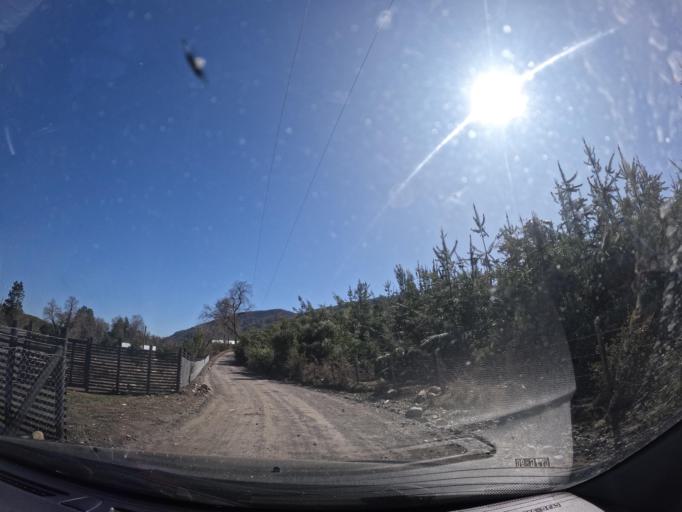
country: CL
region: Maule
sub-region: Provincia de Linares
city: Longavi
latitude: -36.2311
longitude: -71.3715
